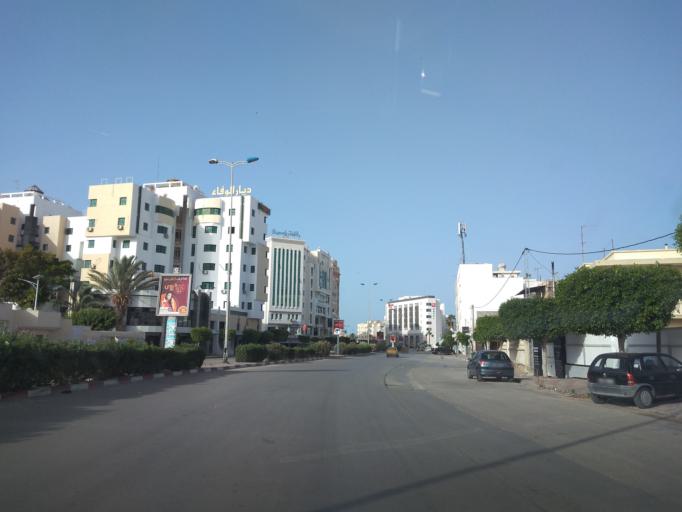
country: TN
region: Safaqis
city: Sfax
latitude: 34.7385
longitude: 10.7507
